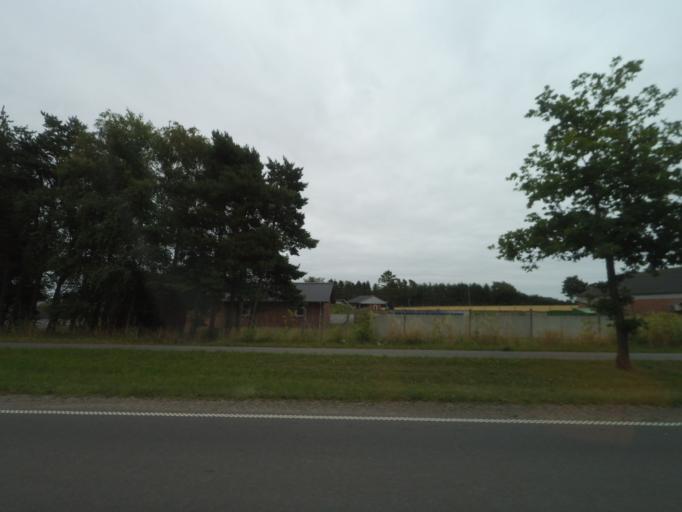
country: DK
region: South Denmark
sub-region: Nordfyns Kommune
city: Otterup
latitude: 55.5217
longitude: 10.4137
